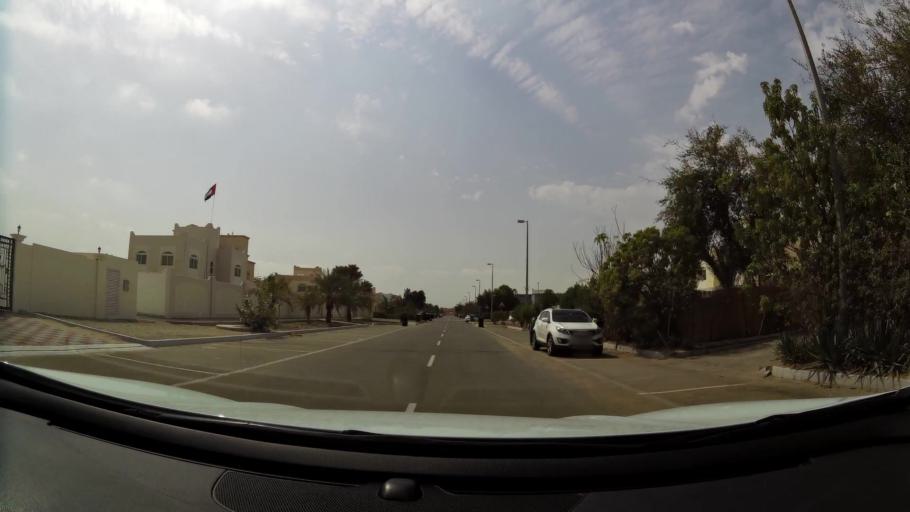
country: AE
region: Abu Dhabi
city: Abu Dhabi
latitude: 24.5465
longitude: 54.6338
